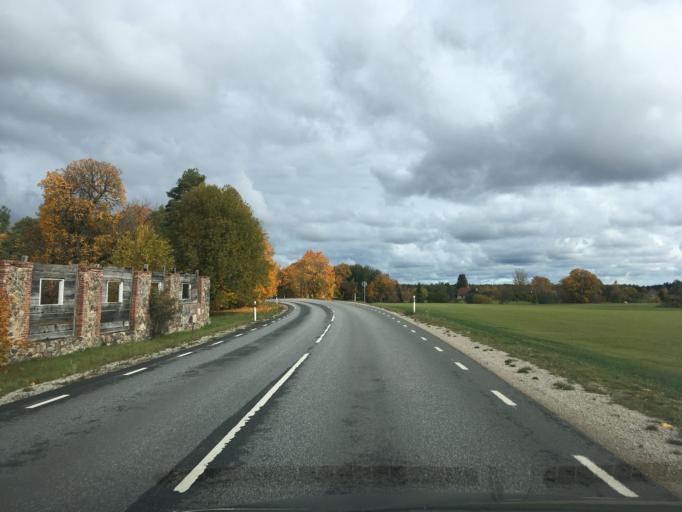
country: EE
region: Harju
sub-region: Anija vald
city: Kehra
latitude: 59.2803
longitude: 25.3718
